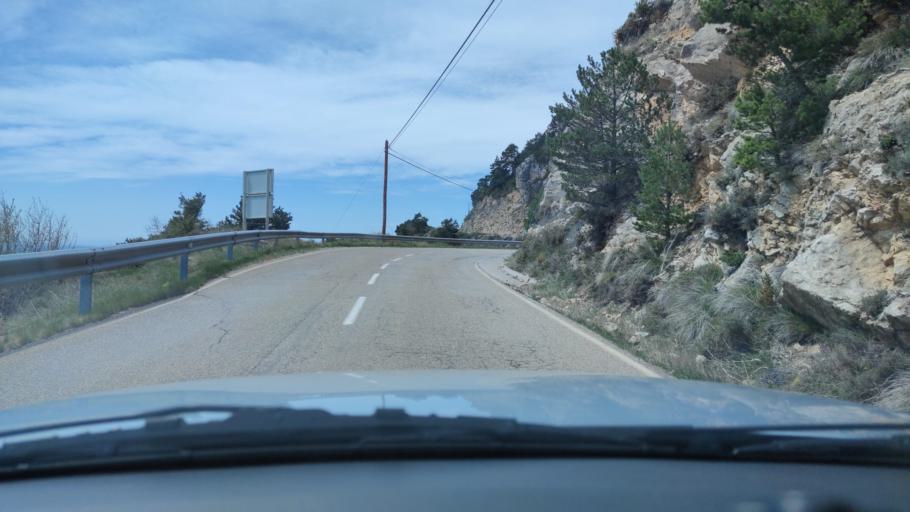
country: ES
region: Catalonia
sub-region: Provincia de Lleida
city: Gosol
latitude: 42.1546
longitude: 1.5718
